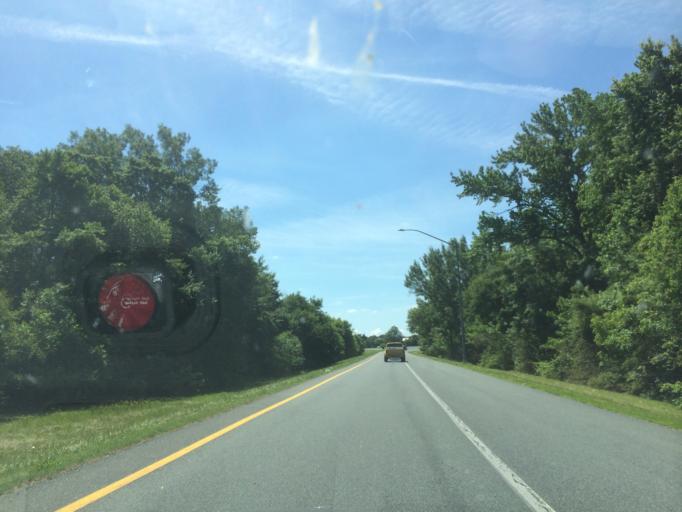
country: US
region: Maryland
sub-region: Wicomico County
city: Salisbury
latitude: 38.3673
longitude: -75.5390
